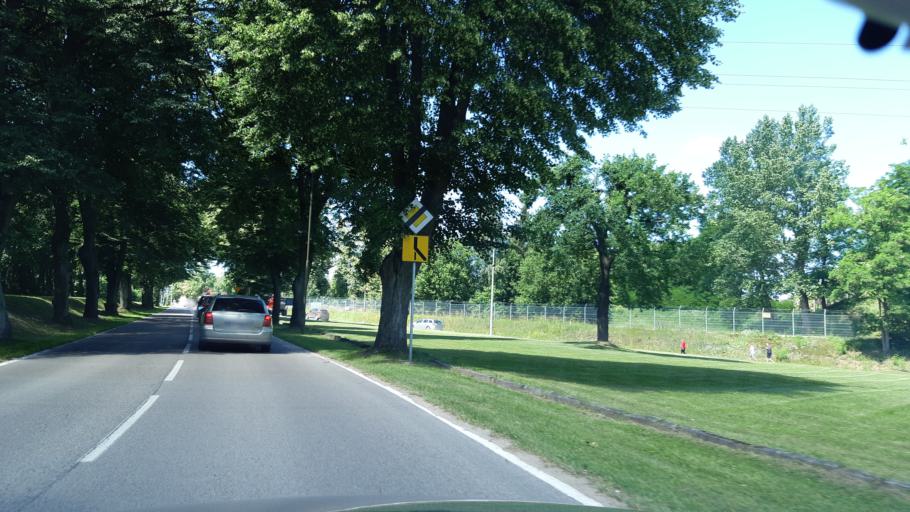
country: PL
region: Warmian-Masurian Voivodeship
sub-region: Powiat gizycki
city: Gizycko
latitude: 54.0370
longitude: 21.7516
